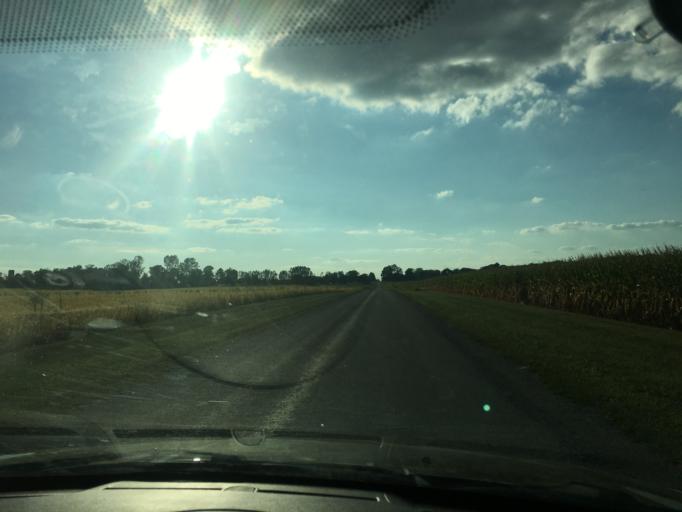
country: US
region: Ohio
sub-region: Logan County
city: West Liberty
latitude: 40.1842
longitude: -83.7442
